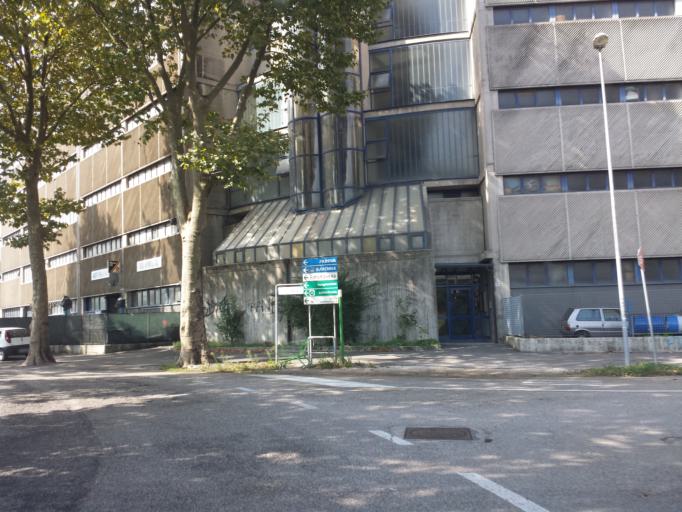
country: IT
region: Veneto
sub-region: Provincia di Venezia
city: Mestre
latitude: 45.4786
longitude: 12.2399
